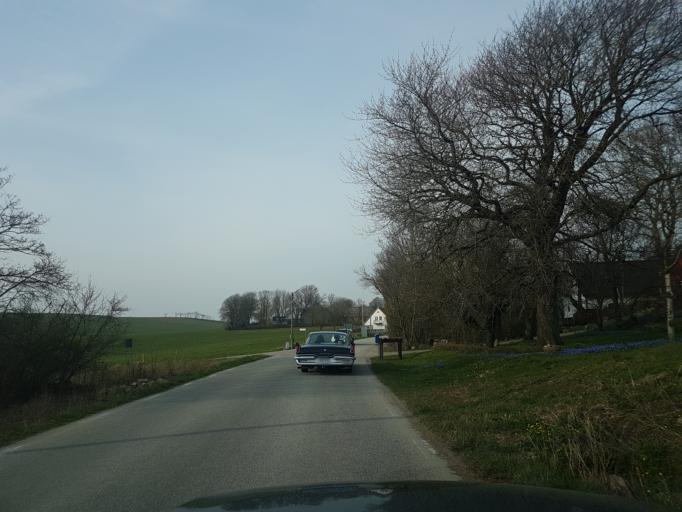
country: SE
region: Skane
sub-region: Ystads Kommun
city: Ystad
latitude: 55.4645
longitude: 13.8225
